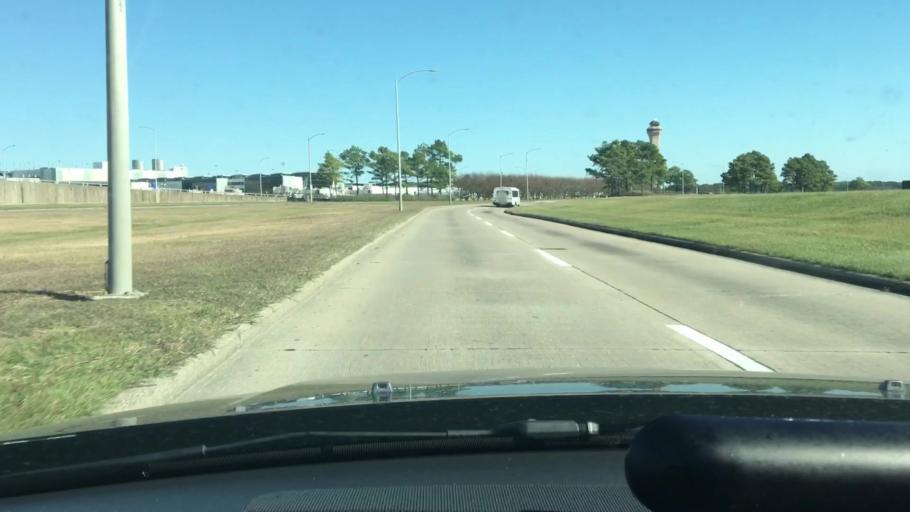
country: US
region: Texas
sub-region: Harris County
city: Aldine
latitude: 29.9809
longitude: -95.3399
